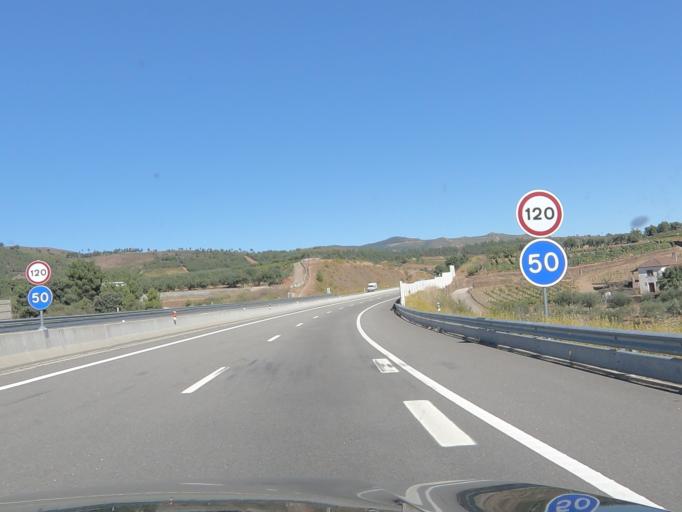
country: PT
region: Vila Real
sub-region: Murca
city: Murca
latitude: 41.3991
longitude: -7.4440
